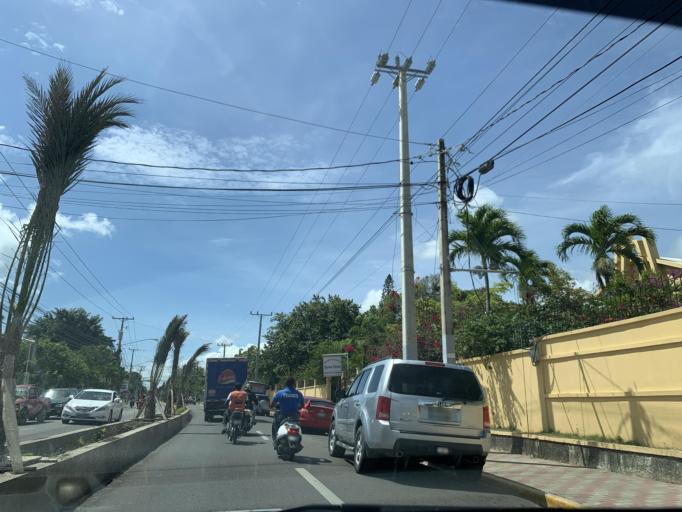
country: DO
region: Puerto Plata
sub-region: Puerto Plata
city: Puerto Plata
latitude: 19.7919
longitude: -70.6819
